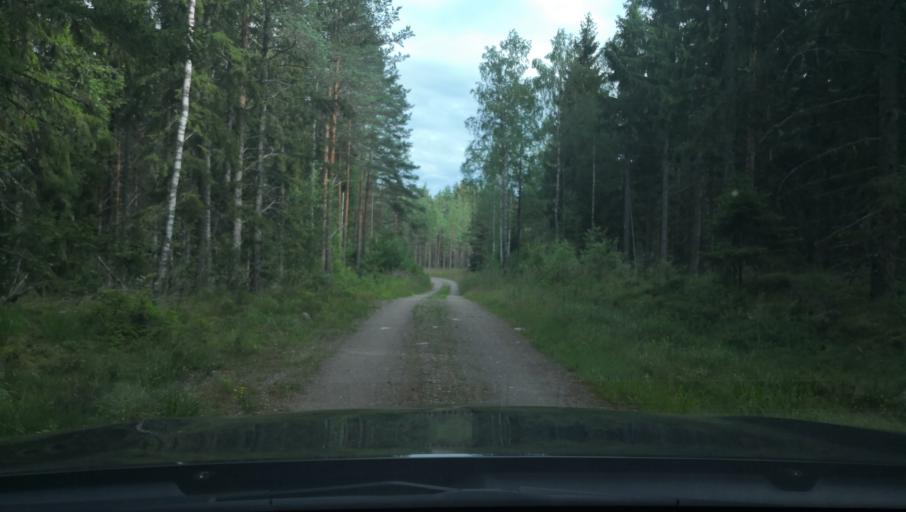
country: SE
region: Vaestmanland
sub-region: Surahammars Kommun
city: Surahammar
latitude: 59.6592
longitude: 16.0955
